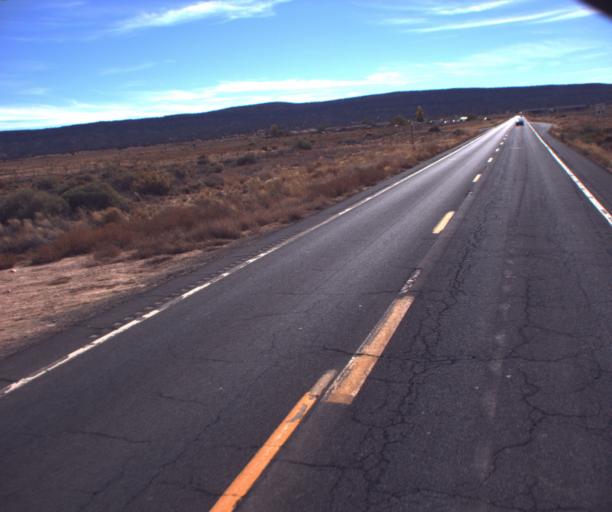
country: US
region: Arizona
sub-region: Coconino County
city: Kaibito
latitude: 36.4683
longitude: -110.6962
